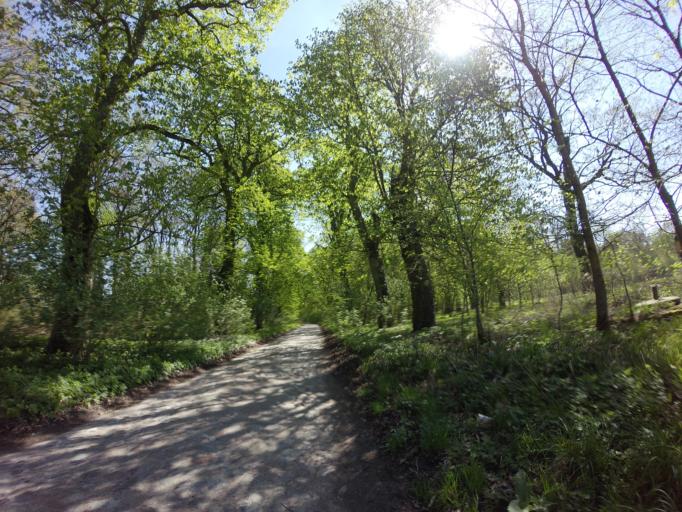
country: PL
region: West Pomeranian Voivodeship
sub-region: Powiat stargardzki
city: Suchan
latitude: 53.1817
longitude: 15.3216
